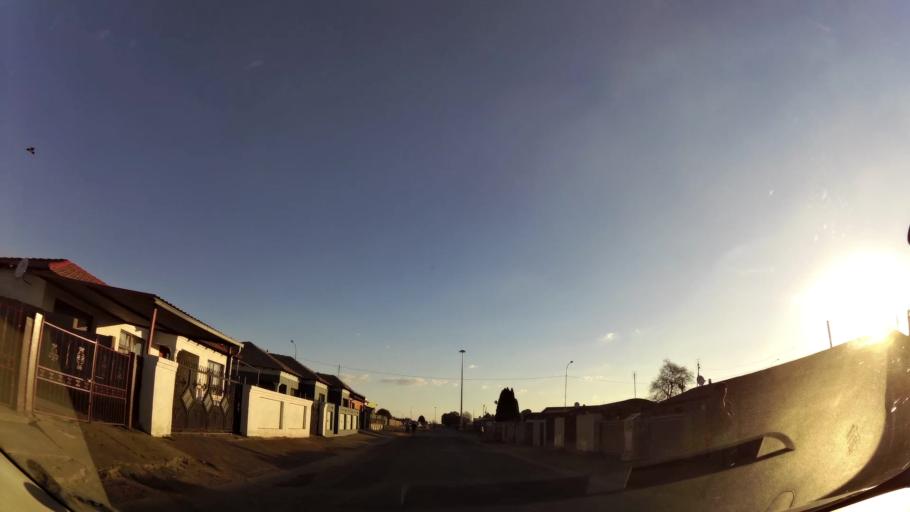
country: ZA
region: Mpumalanga
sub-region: Nkangala District Municipality
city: Witbank
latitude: -25.8785
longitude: 29.1931
